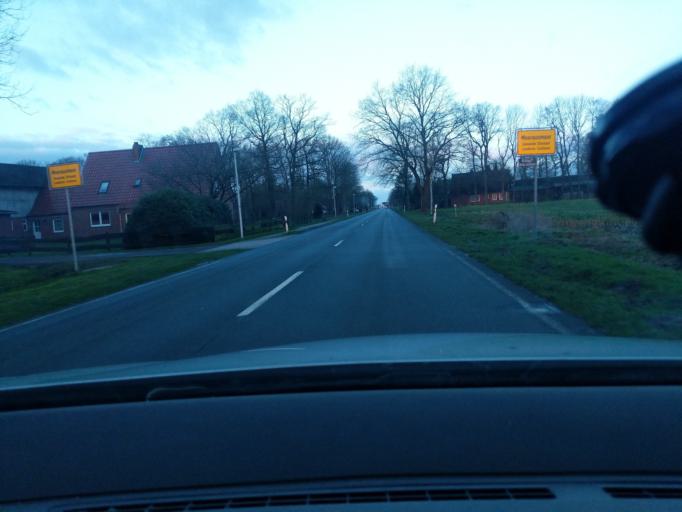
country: DE
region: Lower Saxony
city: Stinstedt
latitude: 53.6344
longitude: 8.9709
